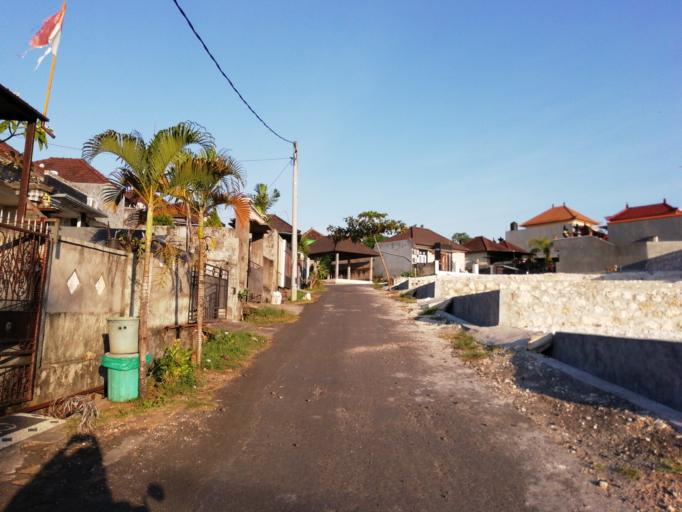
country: ID
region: Bali
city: Bualu
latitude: -8.8001
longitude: 115.1959
